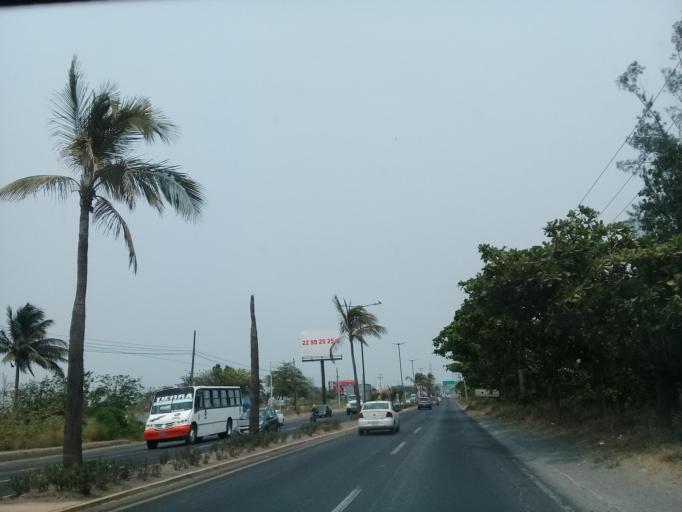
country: MX
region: Veracruz
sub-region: Veracruz
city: Hacienda Sotavento
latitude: 19.1425
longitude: -96.1565
